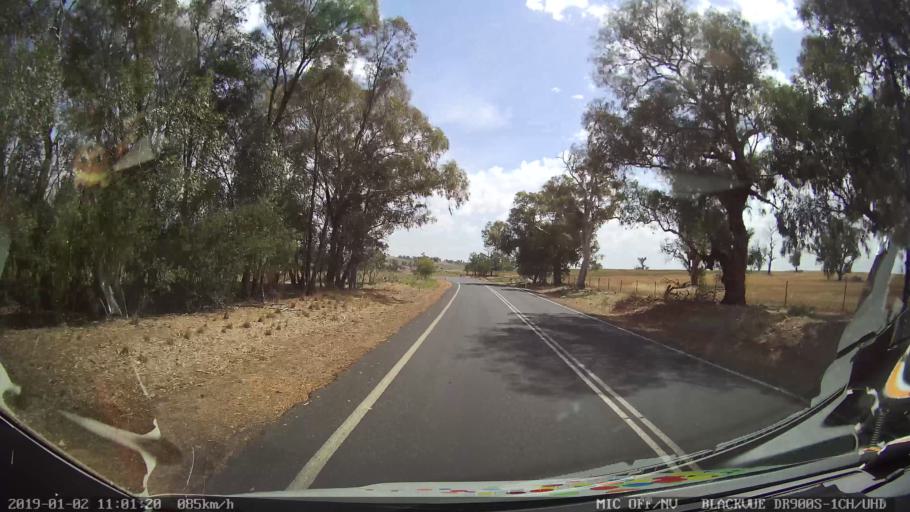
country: AU
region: New South Wales
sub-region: Young
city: Young
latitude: -34.5991
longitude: 148.3193
